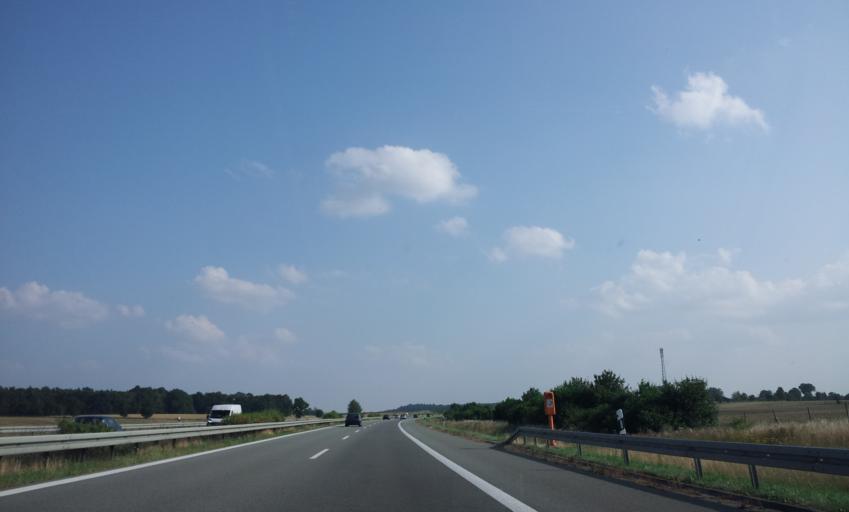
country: DE
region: Mecklenburg-Vorpommern
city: Brunn
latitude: 53.6476
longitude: 13.3685
